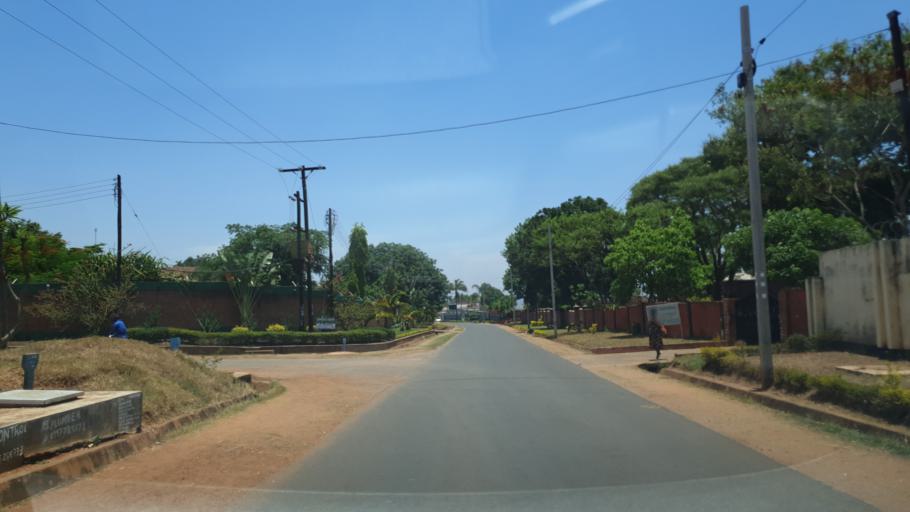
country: MW
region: Central Region
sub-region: Lilongwe District
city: Lilongwe
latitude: -13.9786
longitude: 33.7457
